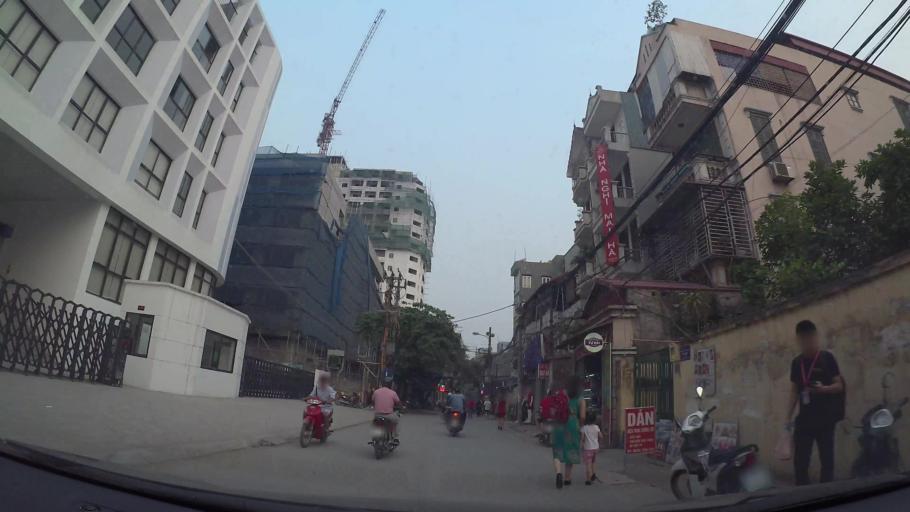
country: VN
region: Ha Noi
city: Thanh Xuan
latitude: 20.9848
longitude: 105.7995
